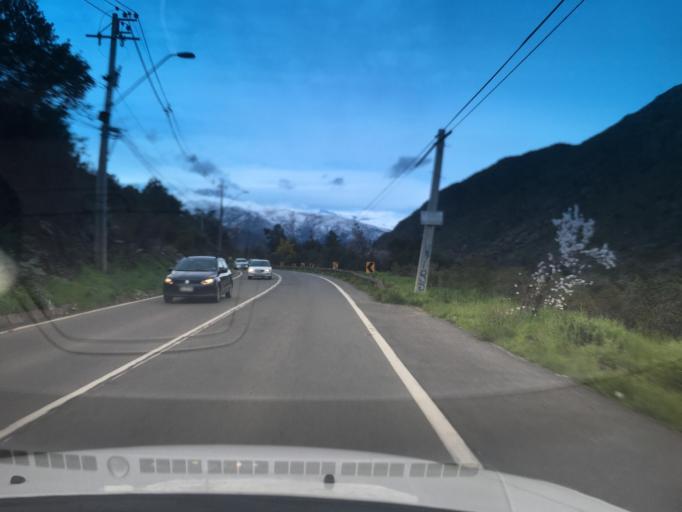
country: CL
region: Santiago Metropolitan
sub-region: Provincia de Cordillera
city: Puente Alto
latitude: -33.5770
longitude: -70.4397
